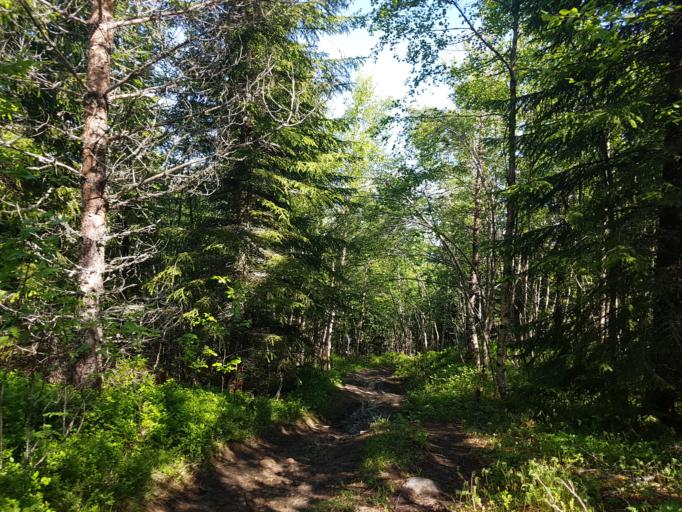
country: NO
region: Sor-Trondelag
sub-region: Trondheim
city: Trondheim
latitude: 63.4211
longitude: 10.2755
